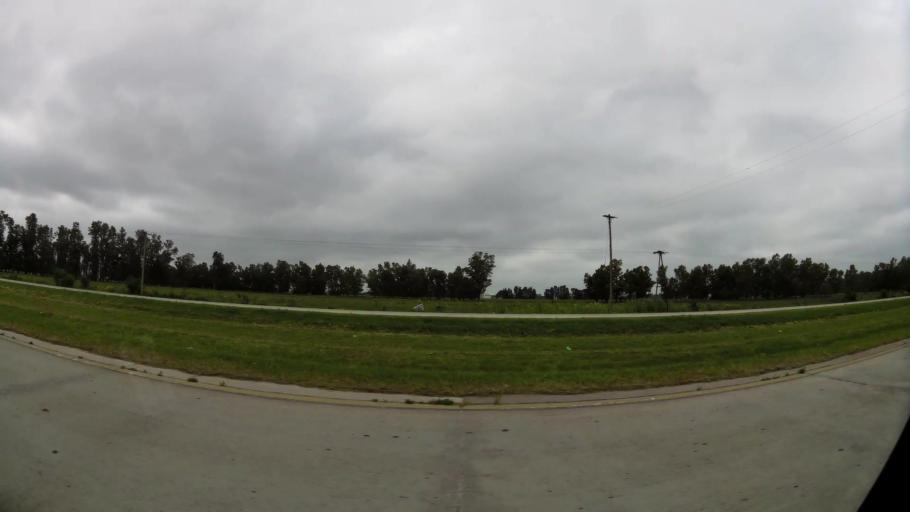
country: AR
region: Buenos Aires
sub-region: Partido de Brandsen
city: Brandsen
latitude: -35.0210
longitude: -58.2600
